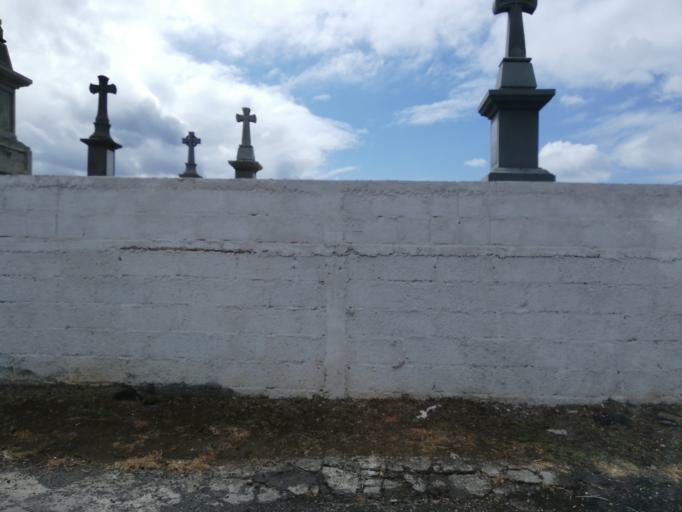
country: MU
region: Port Louis
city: Port Louis
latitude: -20.1614
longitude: 57.4852
